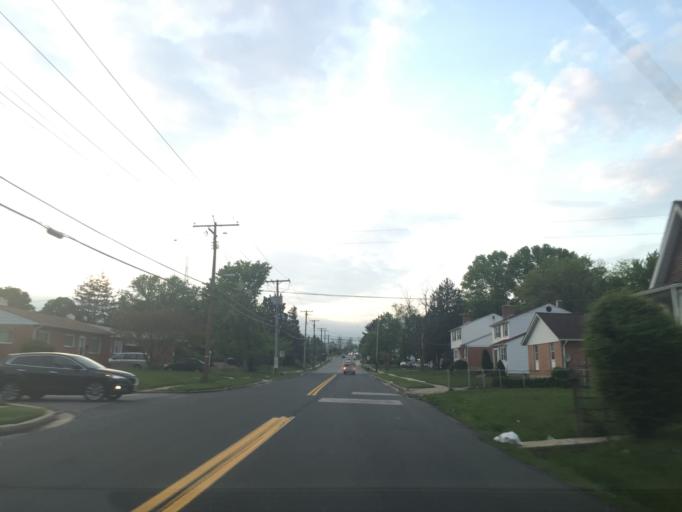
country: US
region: Maryland
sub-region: Baltimore County
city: Parkville
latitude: 39.3841
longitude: -76.5439
